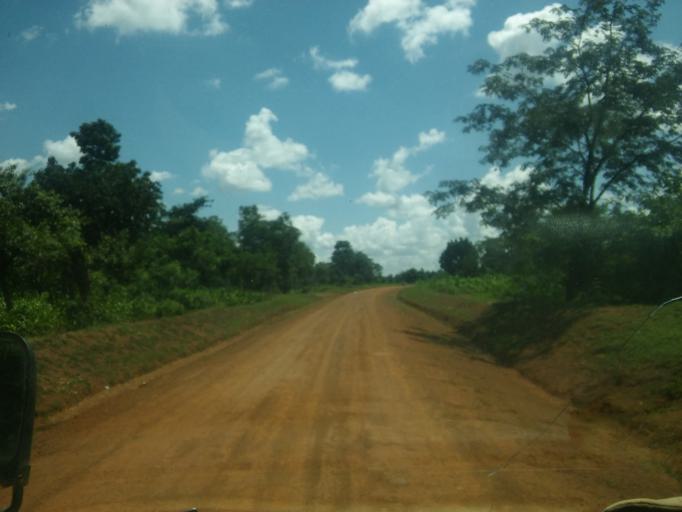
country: UG
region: Eastern Region
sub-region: Budaka District
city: Budaka
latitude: 1.1143
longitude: 33.9478
